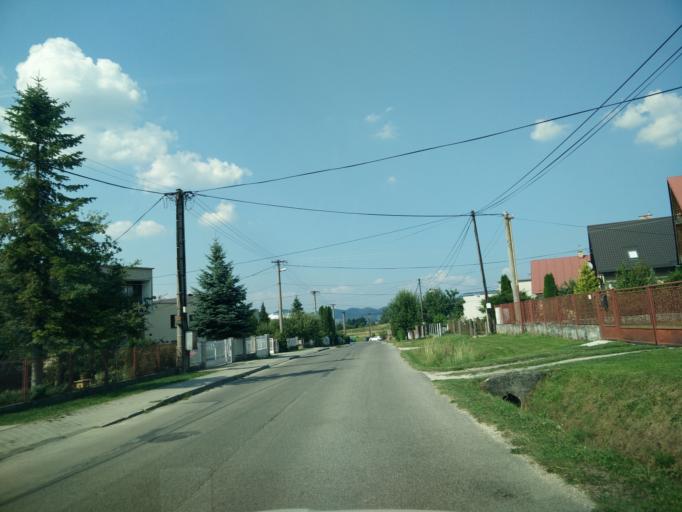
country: SK
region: Zilinsky
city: Rajec
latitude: 49.0802
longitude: 18.6411
